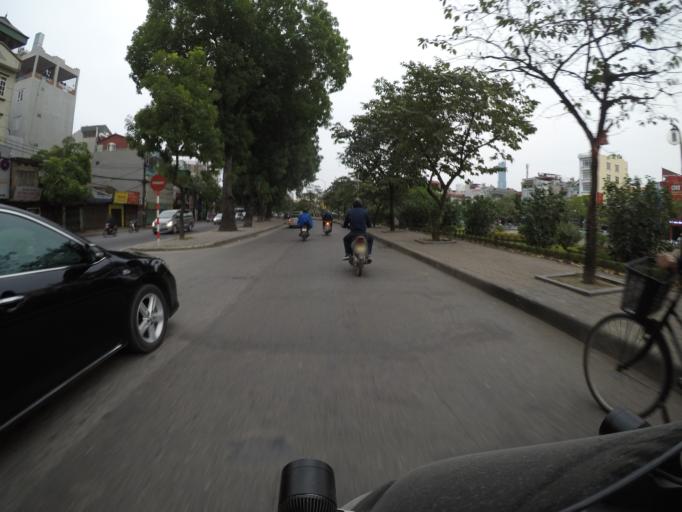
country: VN
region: Ha Noi
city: Cau Giay
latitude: 21.0259
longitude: 105.7983
